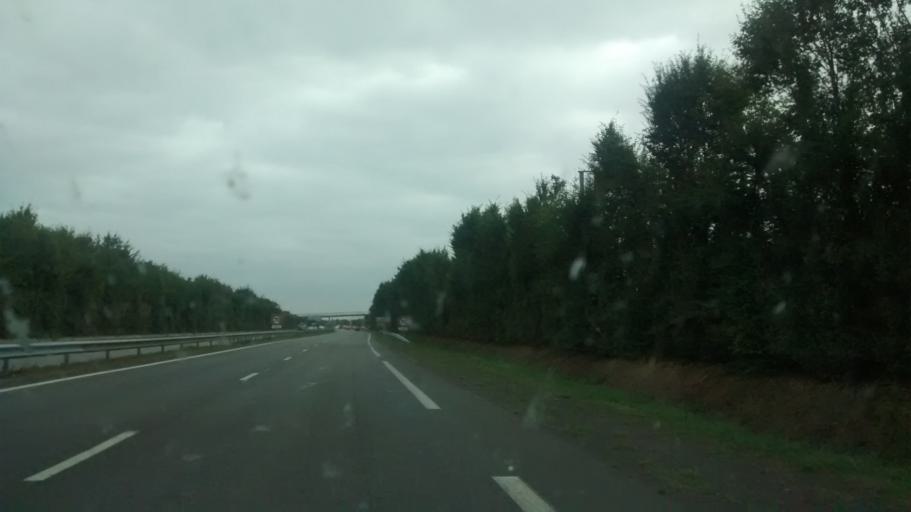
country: FR
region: Brittany
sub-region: Departement d'Ille-et-Vilaine
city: Saint-Jacques-de-la-Lande
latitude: 48.0641
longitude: -1.7177
